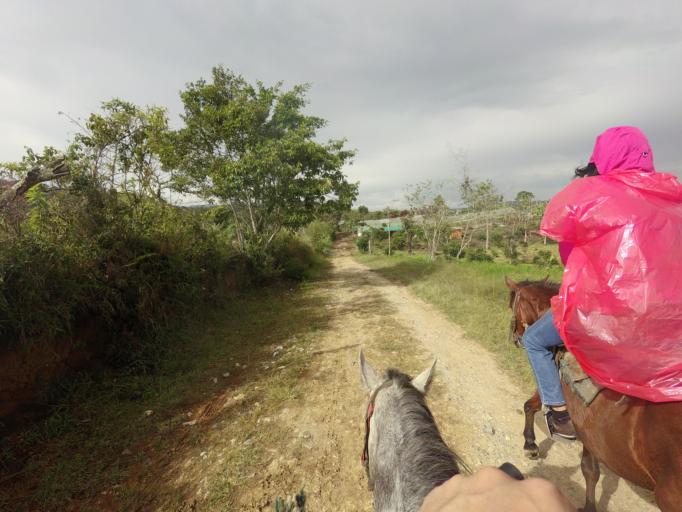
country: CO
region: Huila
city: San Agustin
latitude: 1.9111
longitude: -76.2919
